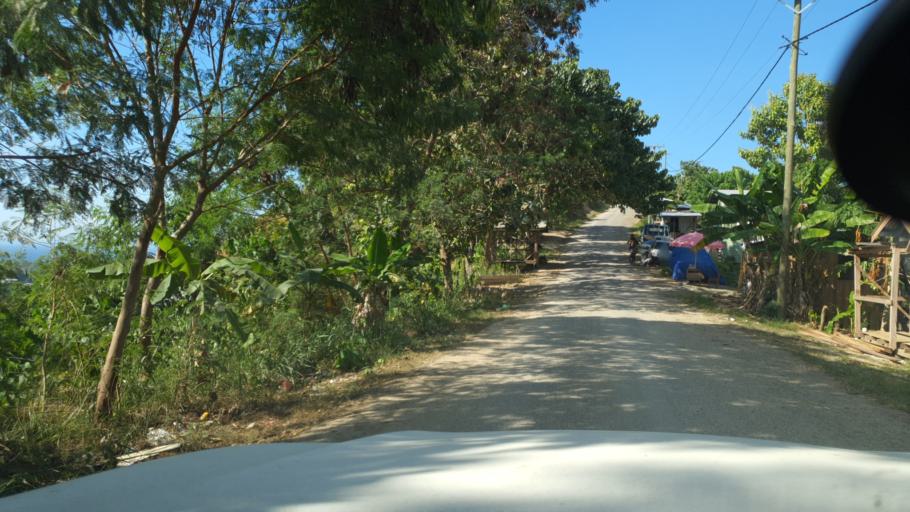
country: SB
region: Guadalcanal
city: Honiara
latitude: -9.4562
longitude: 159.9789
